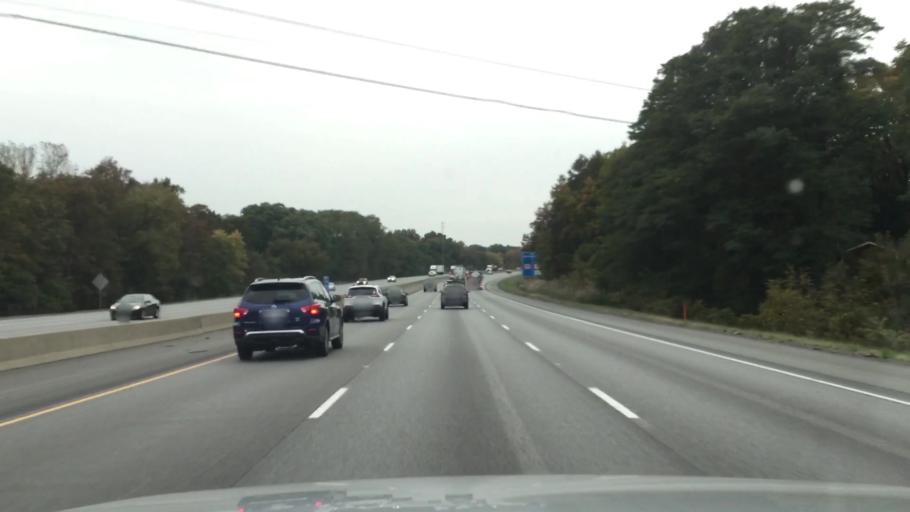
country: US
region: Indiana
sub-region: Porter County
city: Porter
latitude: 41.6124
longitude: -87.0887
